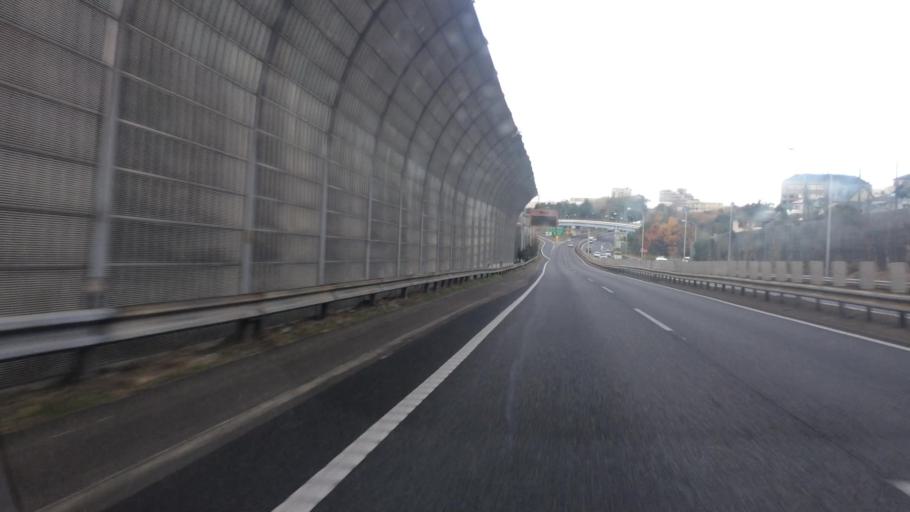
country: JP
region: Hyogo
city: Akashi
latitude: 34.6590
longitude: 135.0312
